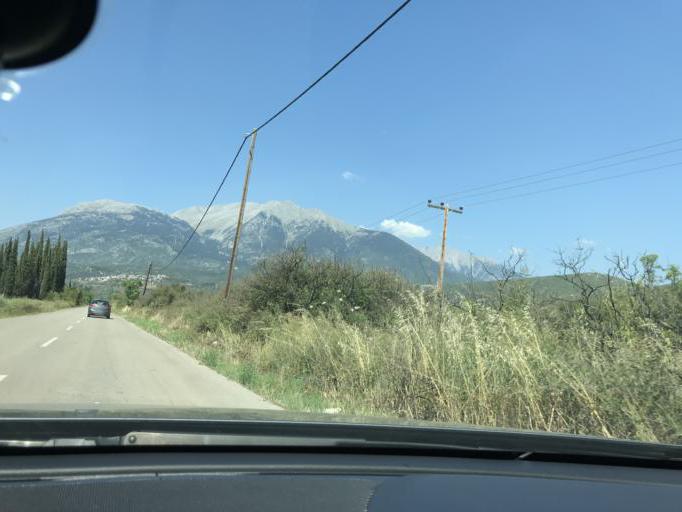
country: GR
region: Central Greece
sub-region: Nomos Fthiotidos
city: Kato Tithorea
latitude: 38.5213
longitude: 22.7740
